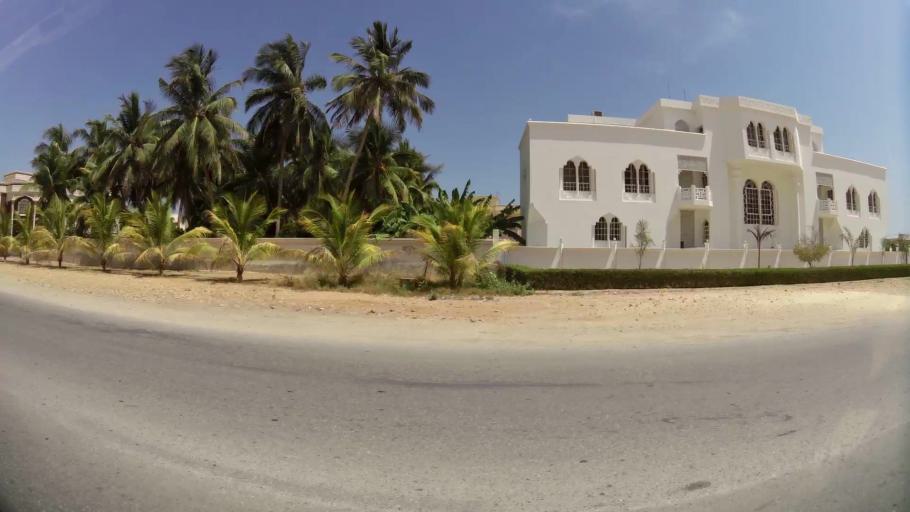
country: OM
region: Zufar
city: Salalah
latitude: 17.0502
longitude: 54.1554
